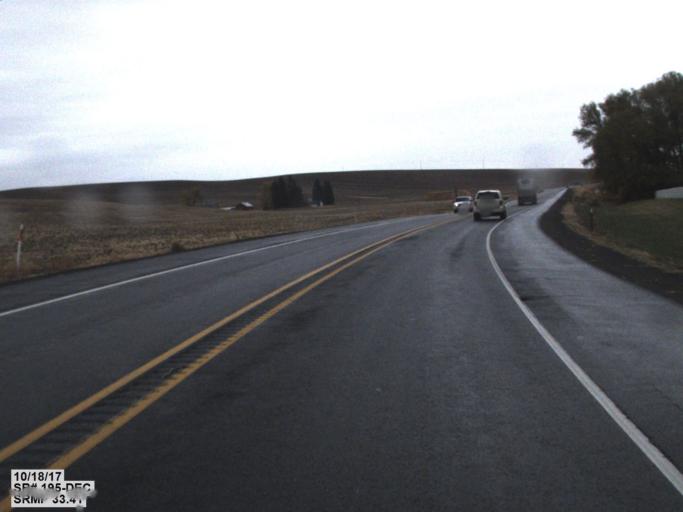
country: US
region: Washington
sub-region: Whitman County
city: Colfax
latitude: 46.8303
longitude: -117.3282
